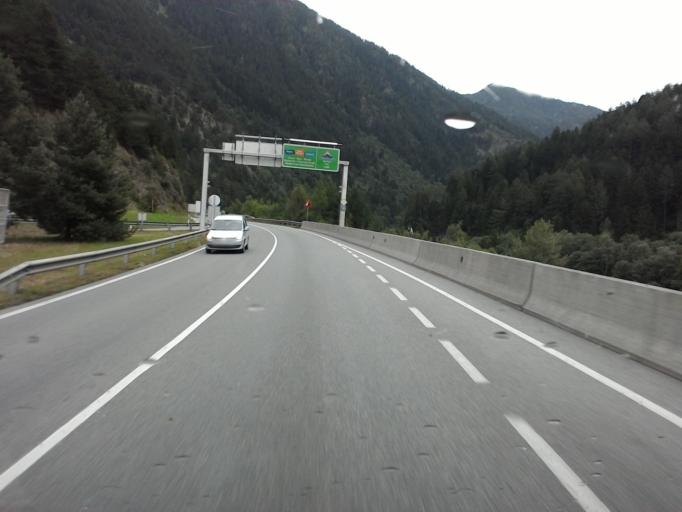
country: AT
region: Tyrol
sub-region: Politischer Bezirk Landeck
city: Prutz
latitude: 47.1139
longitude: 10.6460
